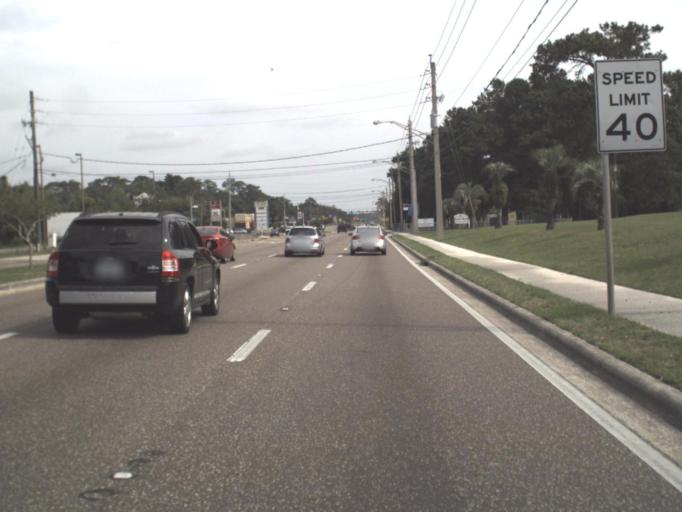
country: US
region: Florida
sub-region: Clay County
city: Orange Park
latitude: 30.1693
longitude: -81.7011
